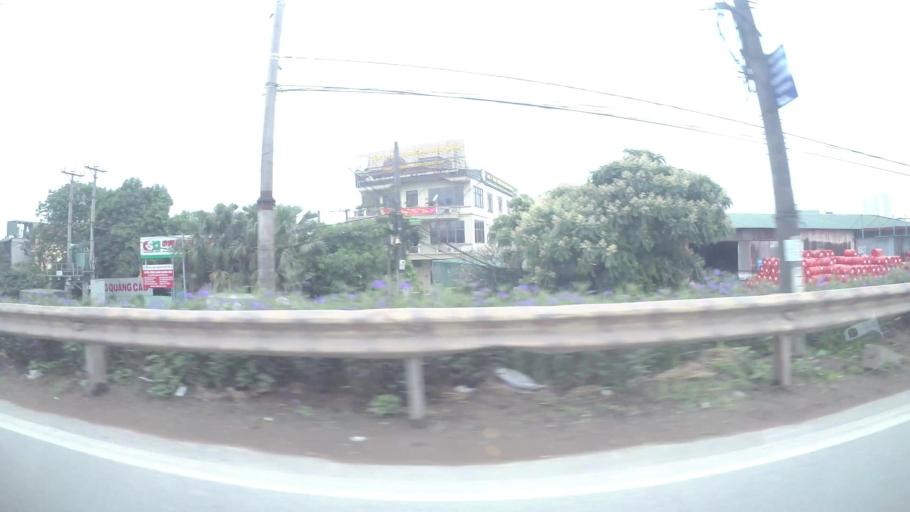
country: VN
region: Ha Noi
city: Hai BaTrung
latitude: 20.9888
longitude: 105.8941
